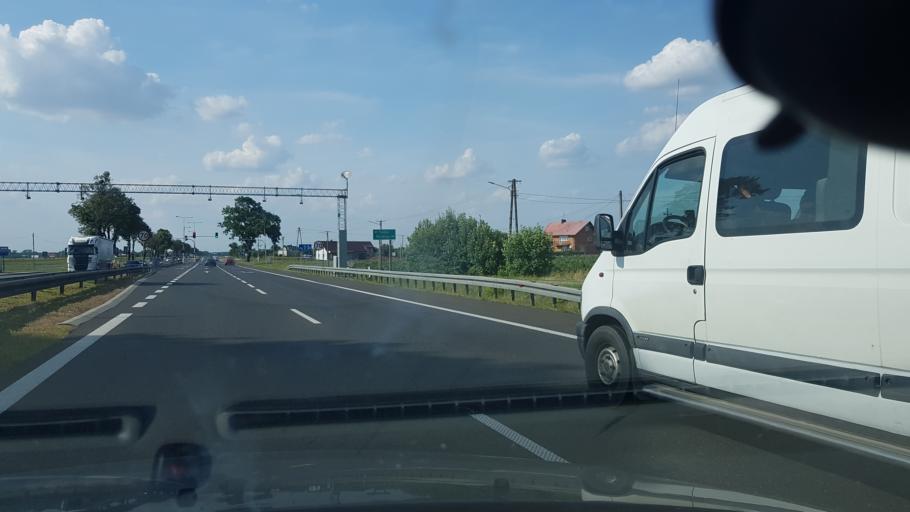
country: PL
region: Masovian Voivodeship
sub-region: Powiat nowodworski
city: Zakroczym
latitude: 52.4601
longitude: 20.5769
